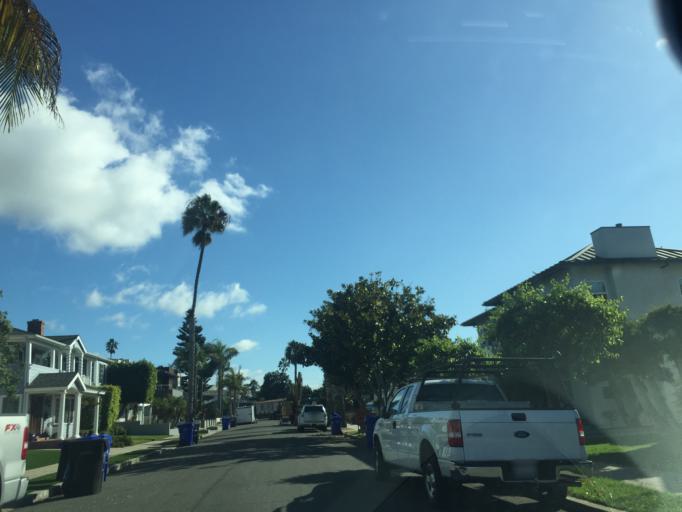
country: US
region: California
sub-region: San Diego County
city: La Jolla
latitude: 32.7816
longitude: -117.2381
